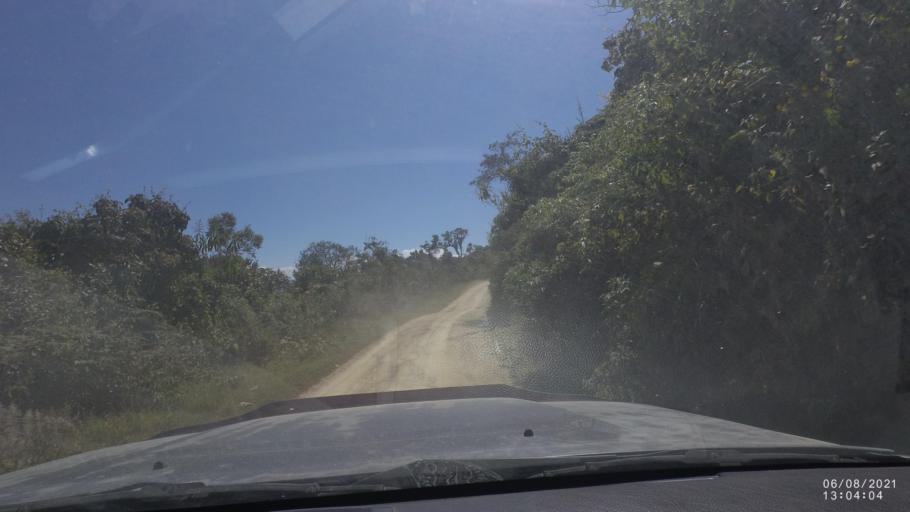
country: BO
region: La Paz
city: Quime
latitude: -16.7388
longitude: -66.6978
